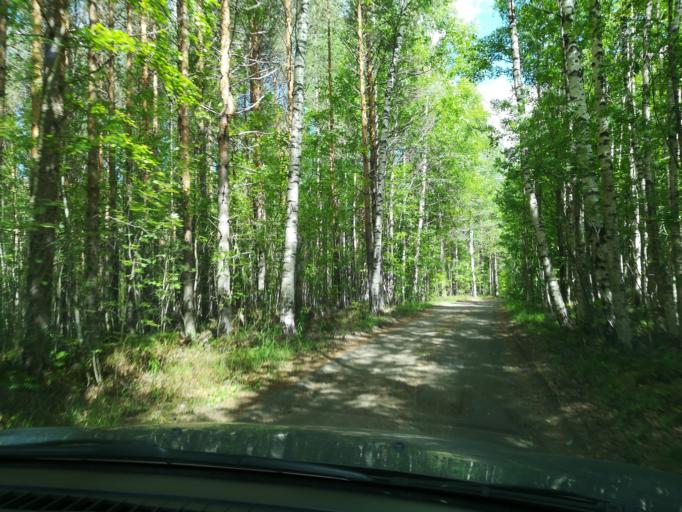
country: FI
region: Southern Savonia
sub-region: Mikkeli
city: Hirvensalmi
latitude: 61.6509
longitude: 26.7782
